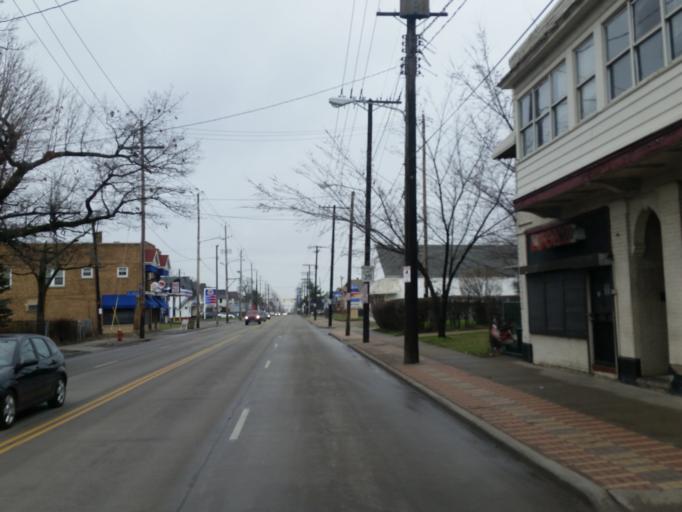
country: US
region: Ohio
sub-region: Cuyahoga County
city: Garfield Heights
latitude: 41.4662
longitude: -81.5938
